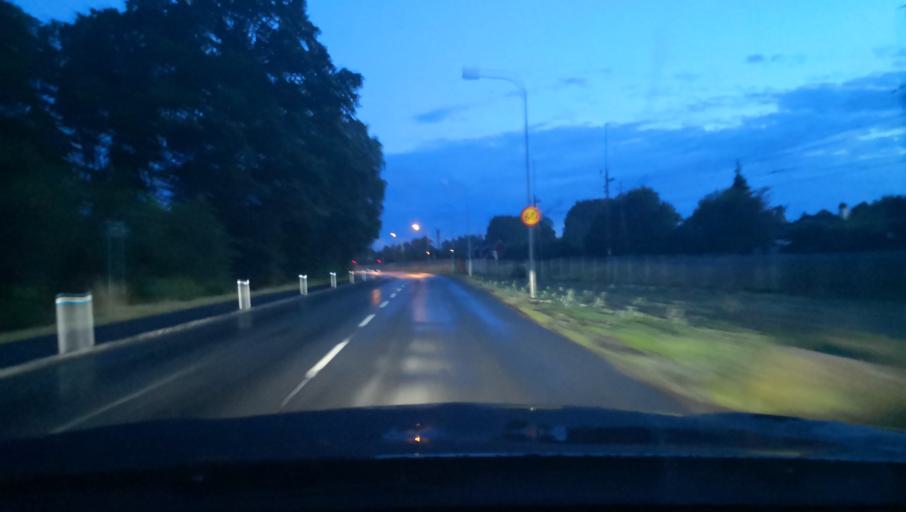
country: SE
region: Skane
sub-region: Osby Kommun
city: Osby
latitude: 56.3756
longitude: 13.9904
